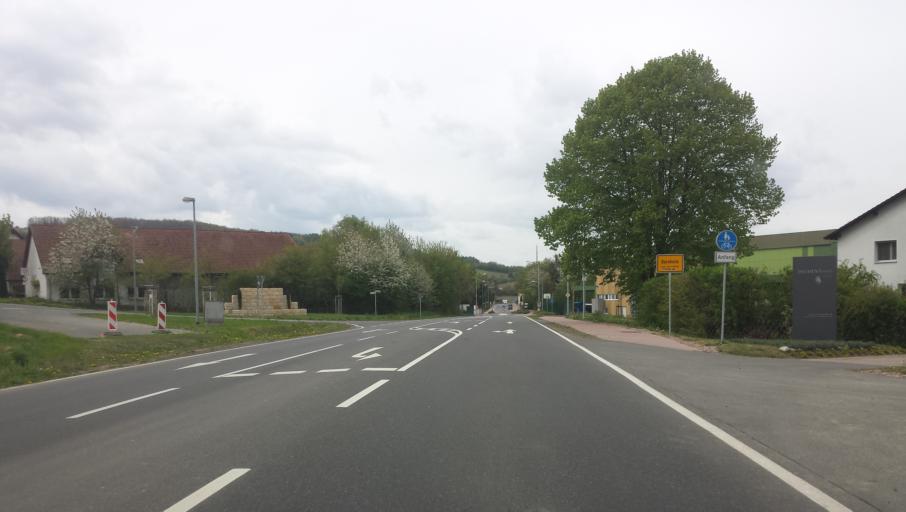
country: DE
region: Rheinland-Pfalz
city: Bornheim
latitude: 49.7837
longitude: 8.0662
